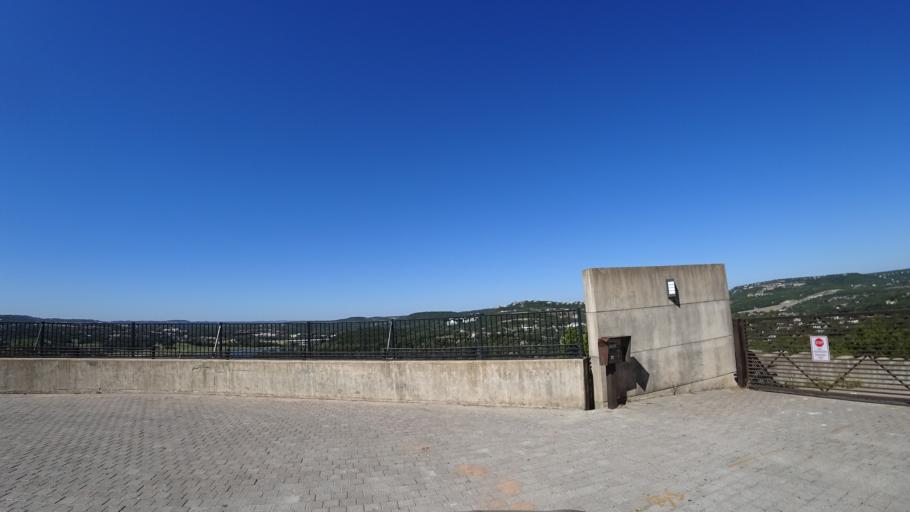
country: US
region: Texas
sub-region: Travis County
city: West Lake Hills
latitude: 30.3496
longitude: -97.7833
